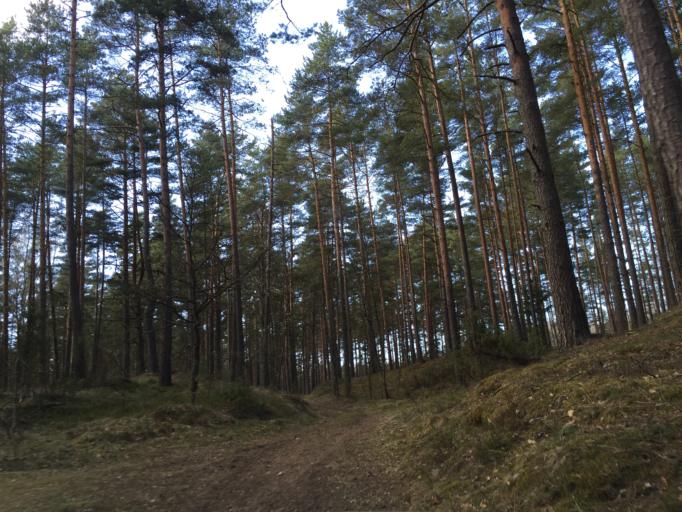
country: LV
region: Riga
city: Bergi
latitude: 57.0012
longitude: 24.2974
